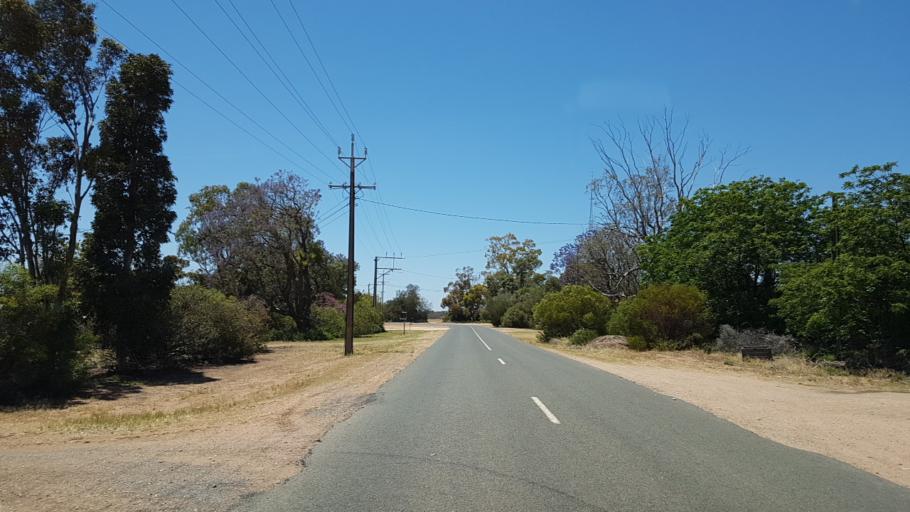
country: AU
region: South Australia
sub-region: Loxton Waikerie
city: Waikerie
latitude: -34.1693
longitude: 140.0356
